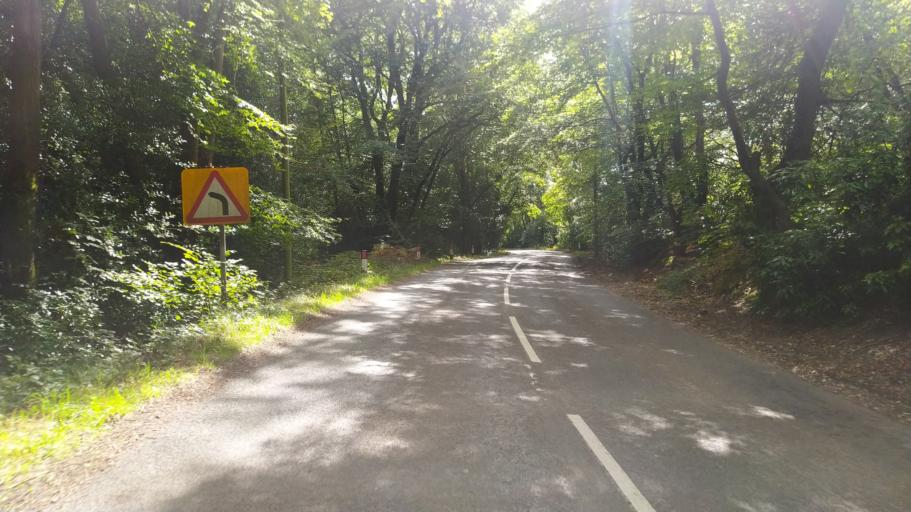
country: GB
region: England
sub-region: Hampshire
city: West Wellow
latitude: 51.0032
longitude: -1.5470
